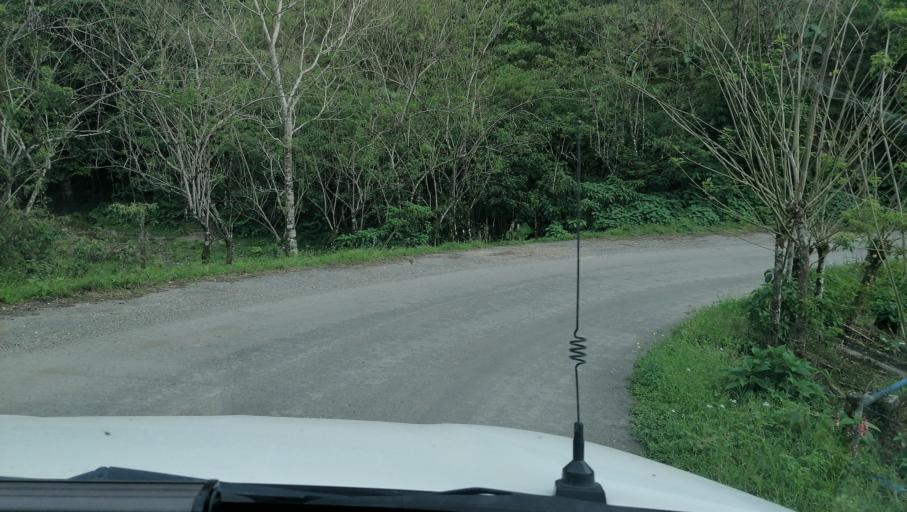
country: MX
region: Chiapas
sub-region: Francisco Leon
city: San Miguel la Sardina
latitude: 17.2408
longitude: -93.2985
